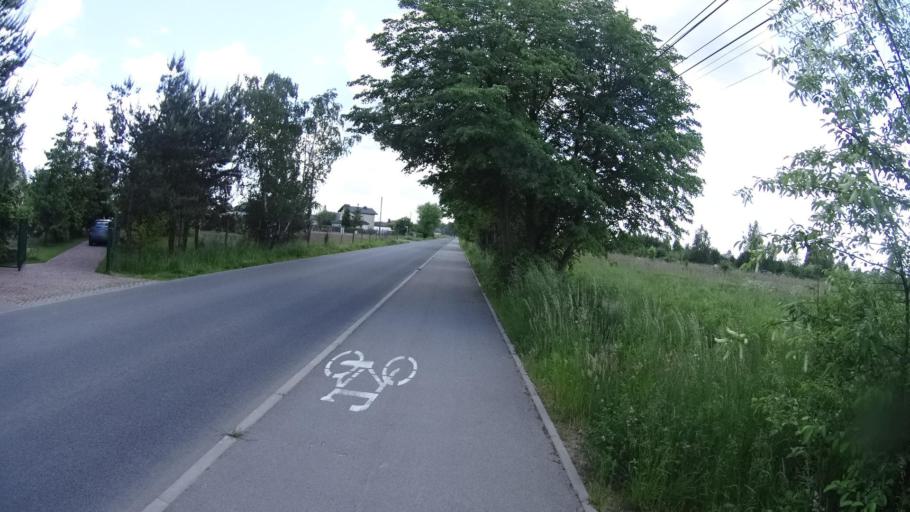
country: PL
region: Masovian Voivodeship
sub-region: Powiat pruszkowski
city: Nadarzyn
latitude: 52.0874
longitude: 20.8156
